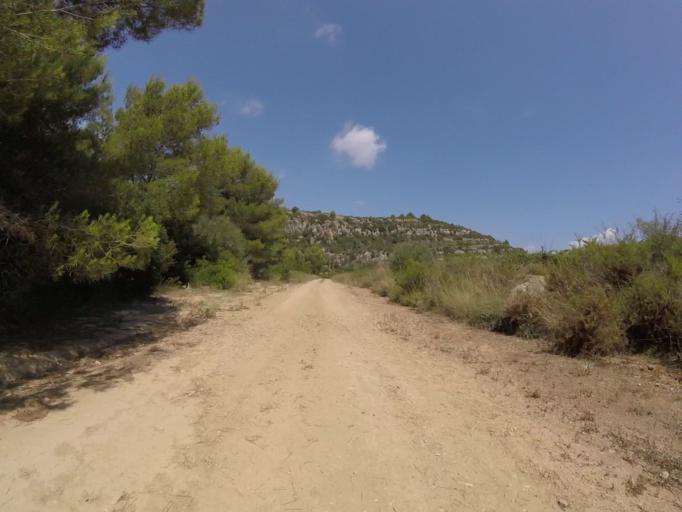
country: ES
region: Valencia
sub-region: Provincia de Castello
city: Torreblanca
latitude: 40.2202
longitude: 0.1481
